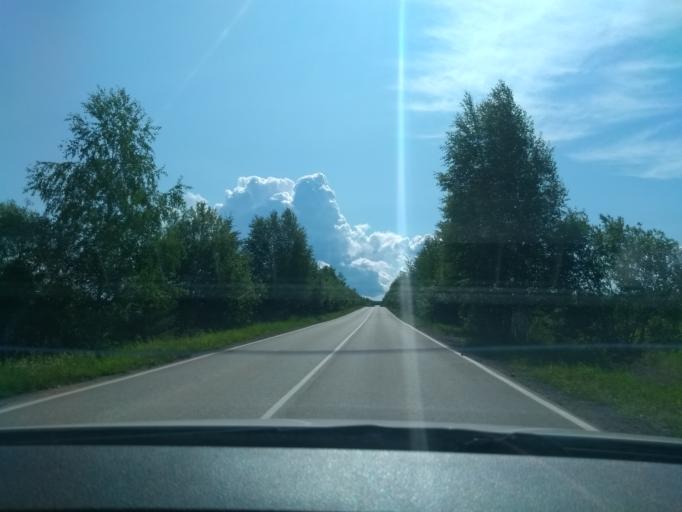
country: RU
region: Perm
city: Bershet'
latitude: 57.8192
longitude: 56.4375
